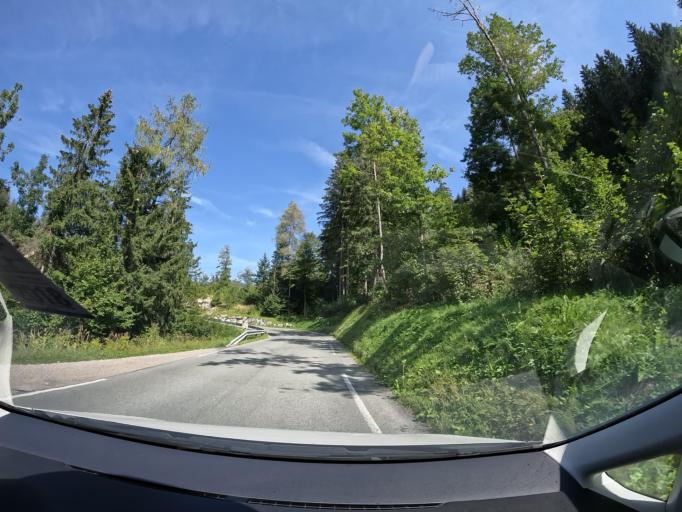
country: AT
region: Carinthia
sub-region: Politischer Bezirk Villach Land
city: Sankt Jakob
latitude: 46.5739
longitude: 14.0795
